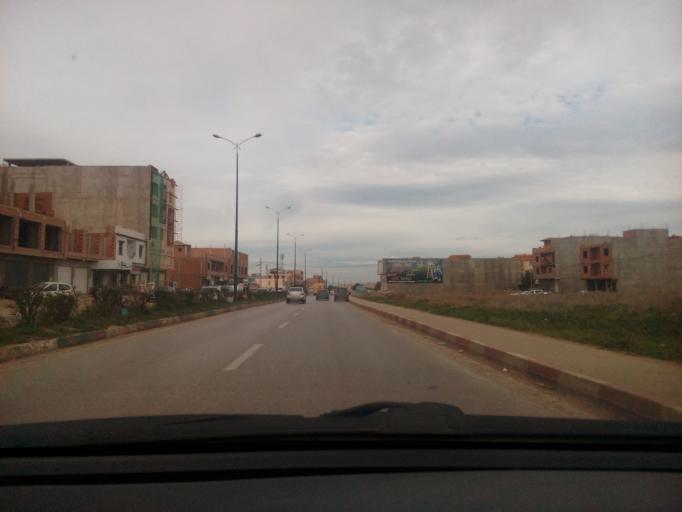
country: DZ
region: Tlemcen
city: Mansoura
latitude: 34.8860
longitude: -1.3529
